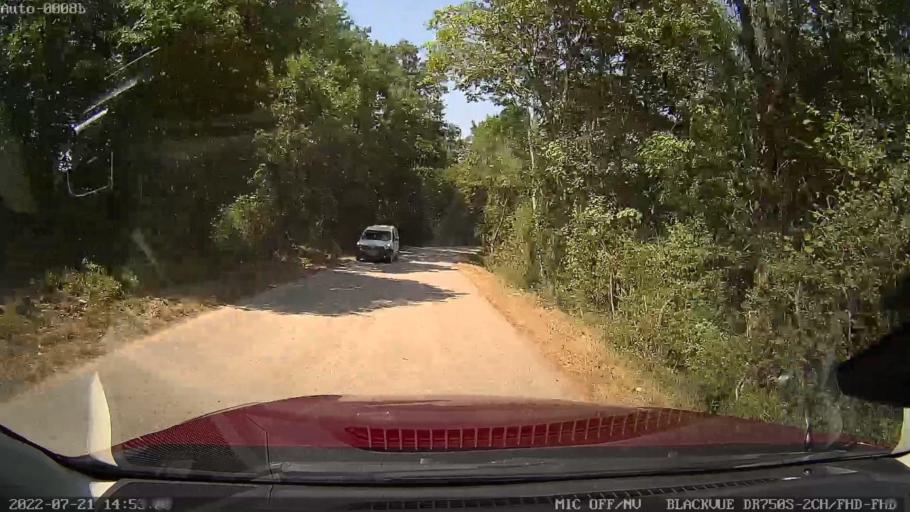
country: HR
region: Istarska
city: Pazin
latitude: 45.1796
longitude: 13.9305
